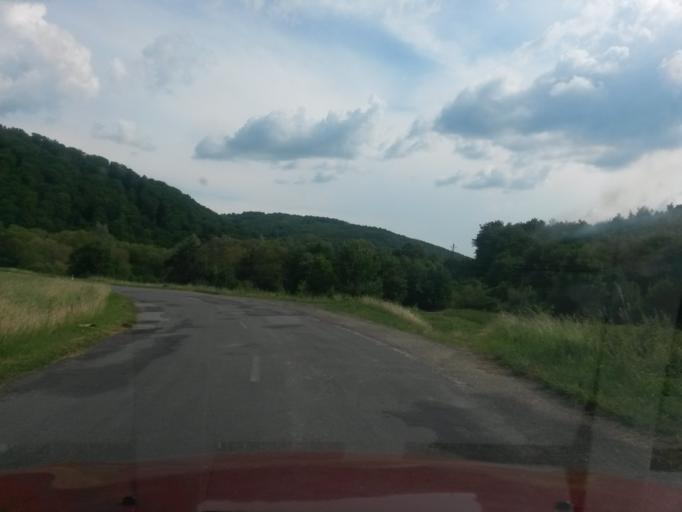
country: SK
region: Presovsky
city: Snina
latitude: 49.1150
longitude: 22.0739
